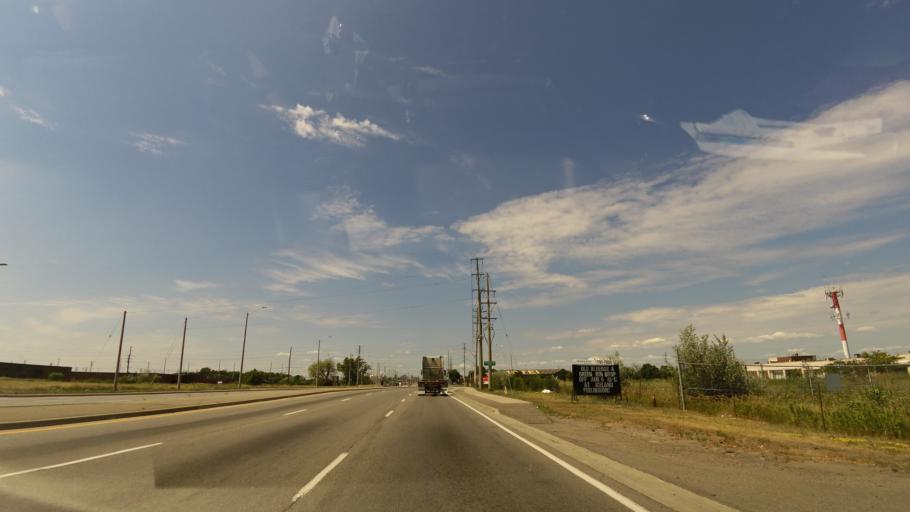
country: CA
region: Ontario
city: Mississauga
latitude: 43.6726
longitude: -79.6708
